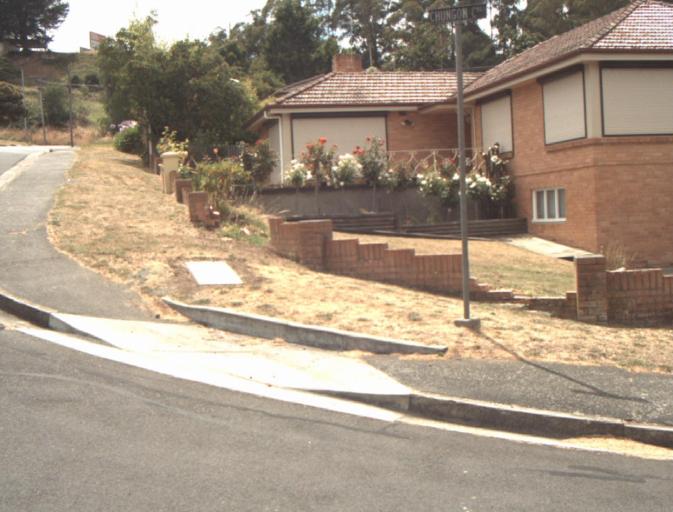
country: AU
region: Tasmania
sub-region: Launceston
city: East Launceston
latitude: -41.4488
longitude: 147.1498
